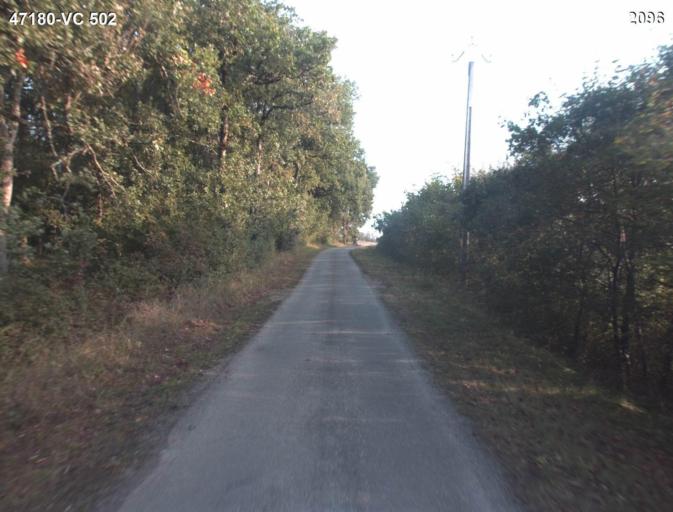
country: FR
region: Aquitaine
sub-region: Departement du Lot-et-Garonne
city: Sainte-Colombe-en-Bruilhois
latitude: 44.1756
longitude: 0.4828
